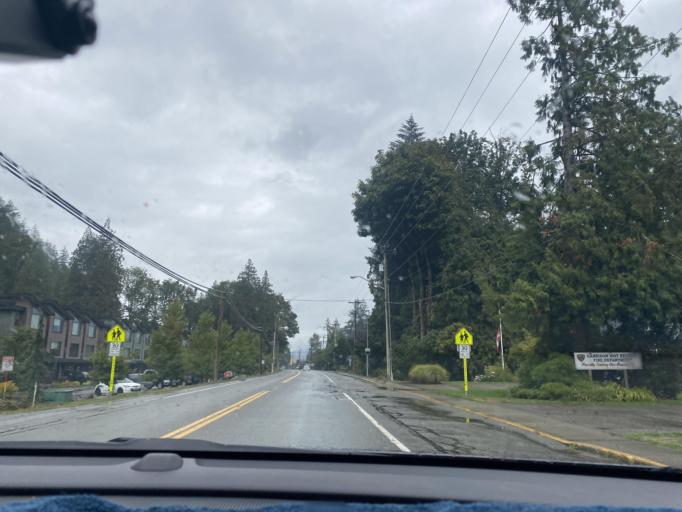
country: CA
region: British Columbia
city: Agassiz
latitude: 49.2966
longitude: -121.7842
